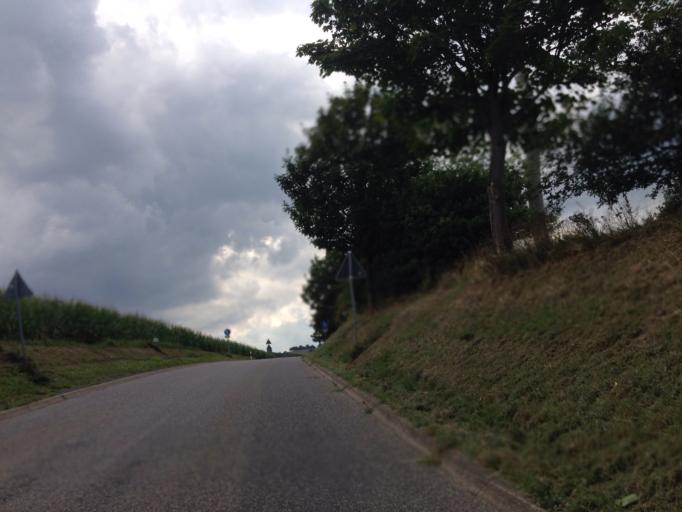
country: DE
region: Hesse
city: Merenberg
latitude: 50.5468
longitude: 8.2110
